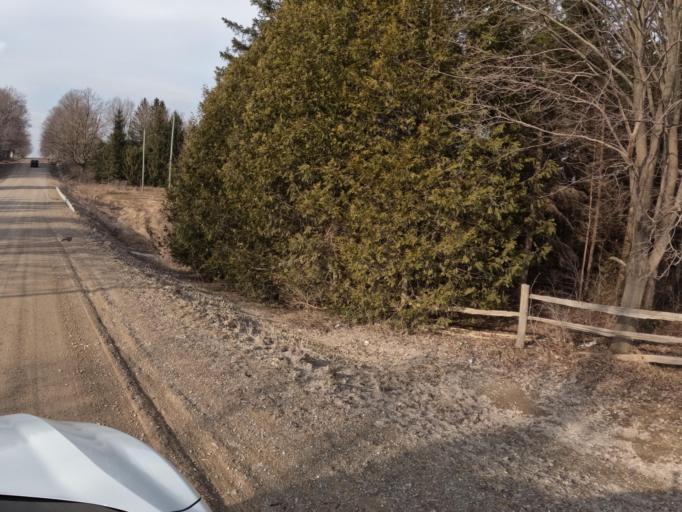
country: CA
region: Ontario
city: Orangeville
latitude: 43.8965
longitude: -80.2669
